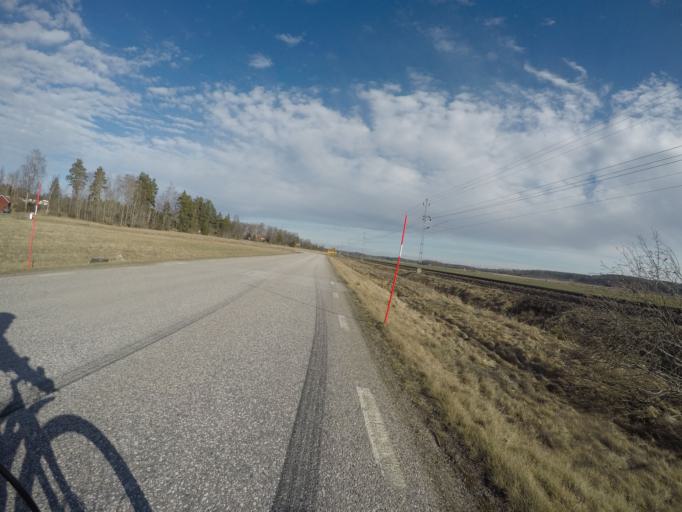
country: SE
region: Vaestmanland
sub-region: Kungsors Kommun
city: Kungsoer
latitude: 59.4198
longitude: 16.1744
